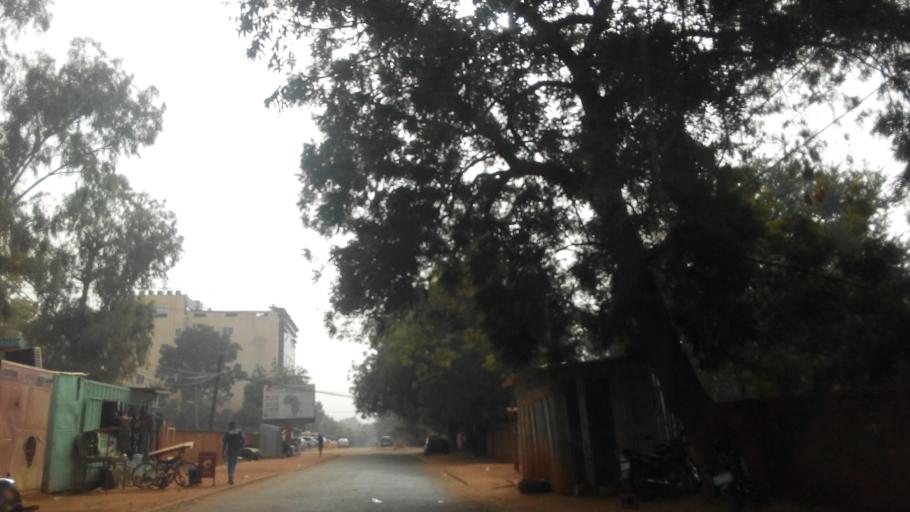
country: NE
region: Niamey
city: Niamey
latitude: 13.5210
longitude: 2.0983
